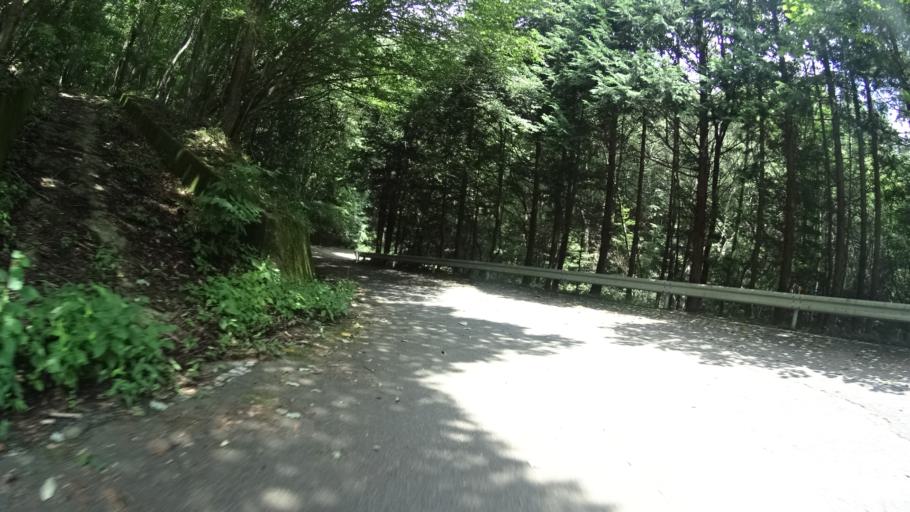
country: JP
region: Yamanashi
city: Nirasaki
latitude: 35.8820
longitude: 138.4998
